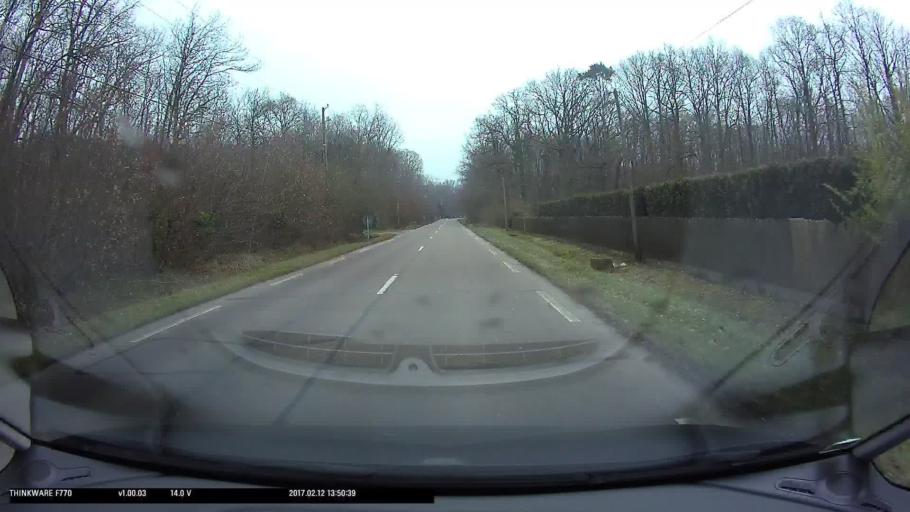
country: FR
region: Ile-de-France
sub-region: Departement des Yvelines
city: Chanteloup-les-Vignes
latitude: 48.9923
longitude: 2.0219
